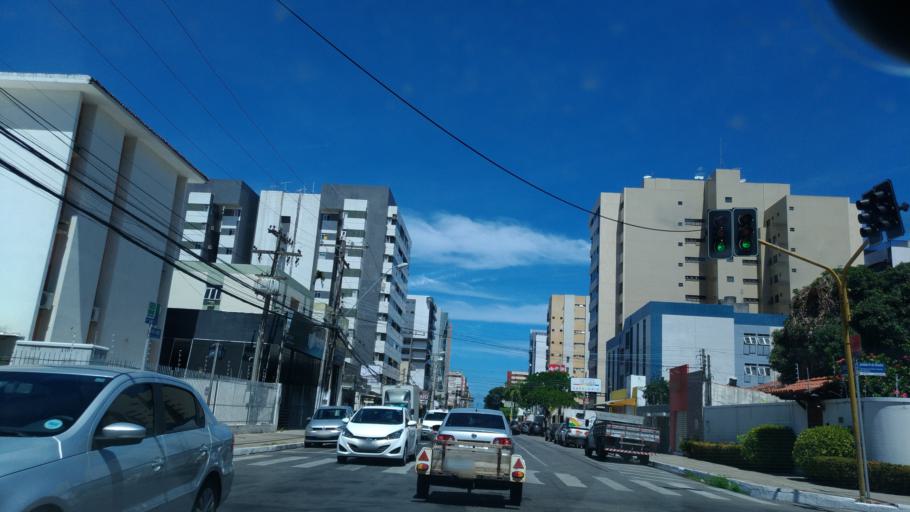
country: BR
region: Alagoas
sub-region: Maceio
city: Maceio
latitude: -9.6567
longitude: -35.7066
